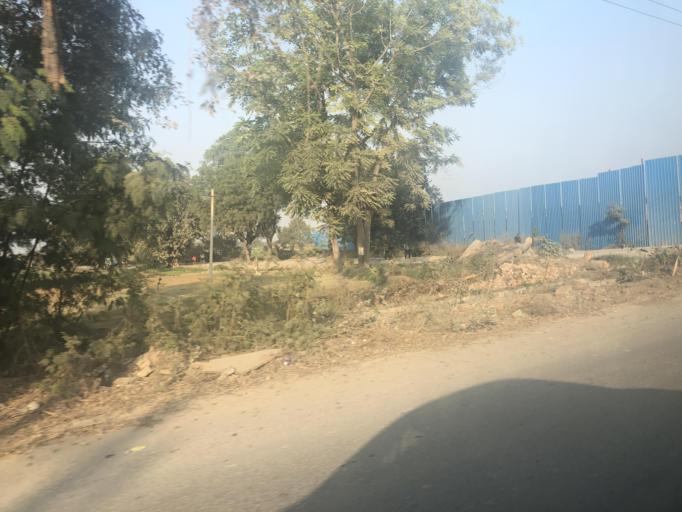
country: IN
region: Haryana
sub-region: Gurgaon
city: Gurgaon
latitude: 28.5382
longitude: 77.0356
